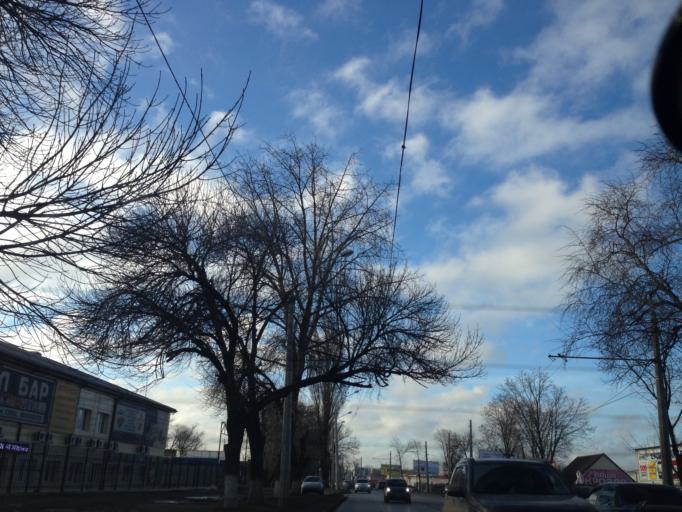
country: RU
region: Rostov
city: Severnyy
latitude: 47.2583
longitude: 39.6325
